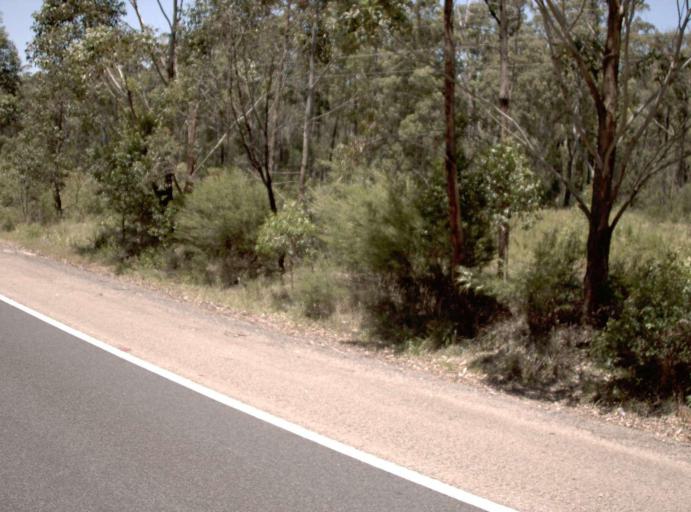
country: AU
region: Victoria
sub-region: East Gippsland
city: Lakes Entrance
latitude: -37.7537
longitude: 148.3252
